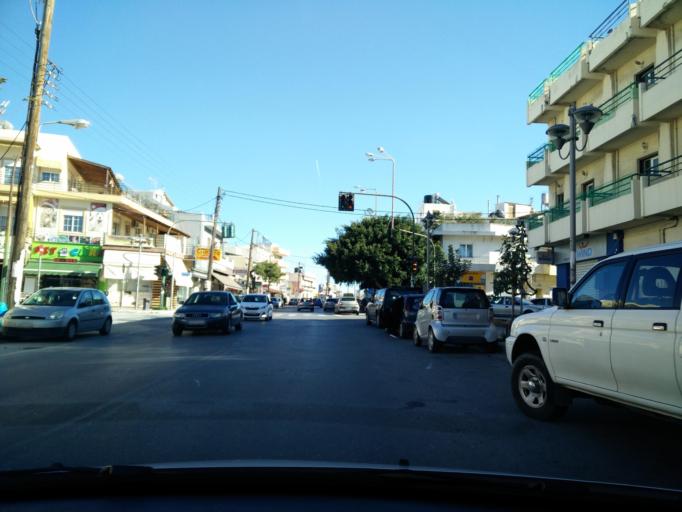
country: GR
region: Crete
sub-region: Nomos Irakleiou
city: Nea Alikarnassos
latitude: 35.3385
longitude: 25.1582
